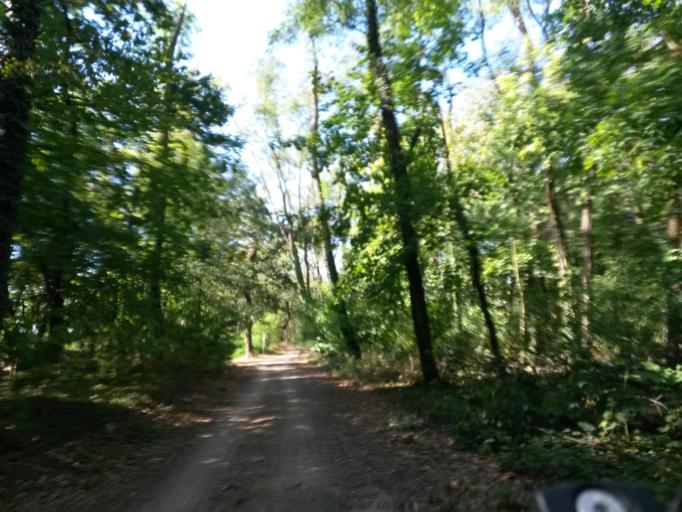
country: DE
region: Saxony-Anhalt
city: Coswig
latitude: 51.8807
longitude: 12.4876
